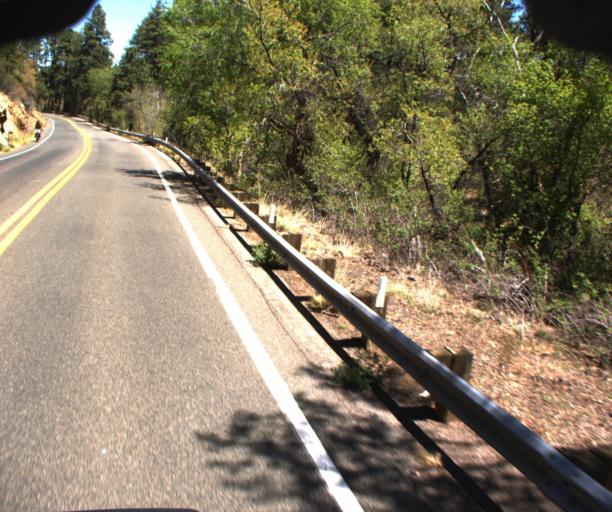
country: US
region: Arizona
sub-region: Yavapai County
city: Prescott
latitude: 34.5063
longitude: -112.4789
